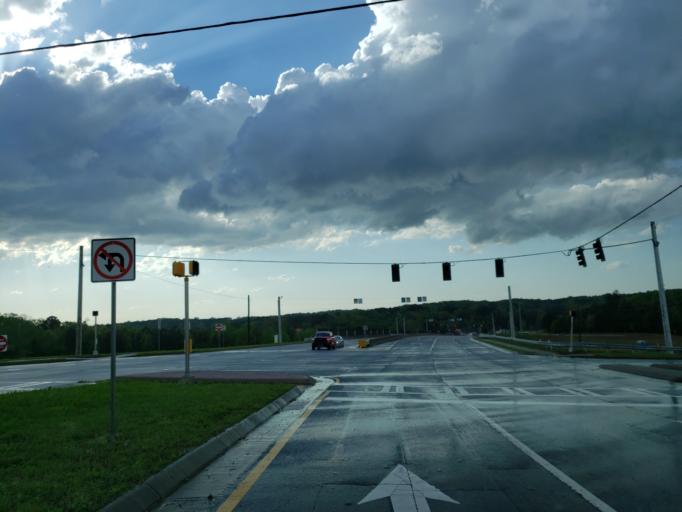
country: US
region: Georgia
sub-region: Cherokee County
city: Holly Springs
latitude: 34.1452
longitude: -84.5153
